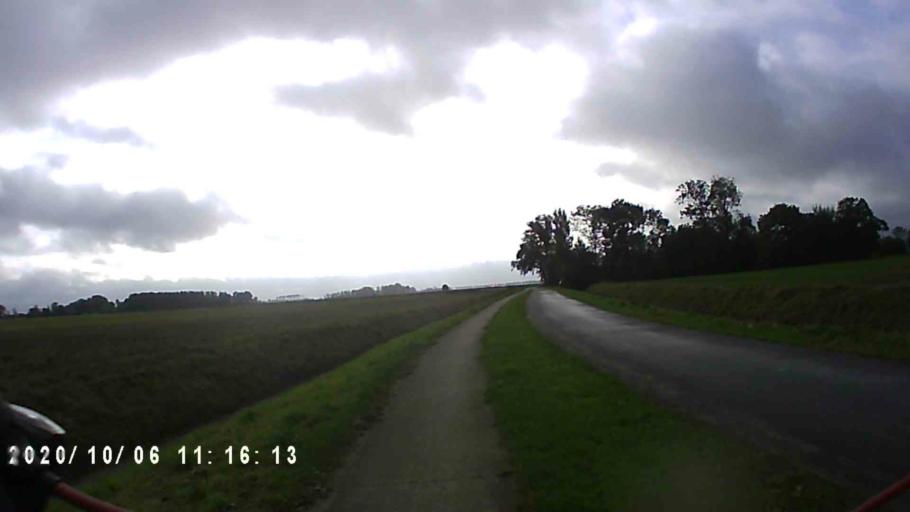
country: NL
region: Groningen
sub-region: Gemeente De Marne
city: Ulrum
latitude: 53.3554
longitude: 6.3813
